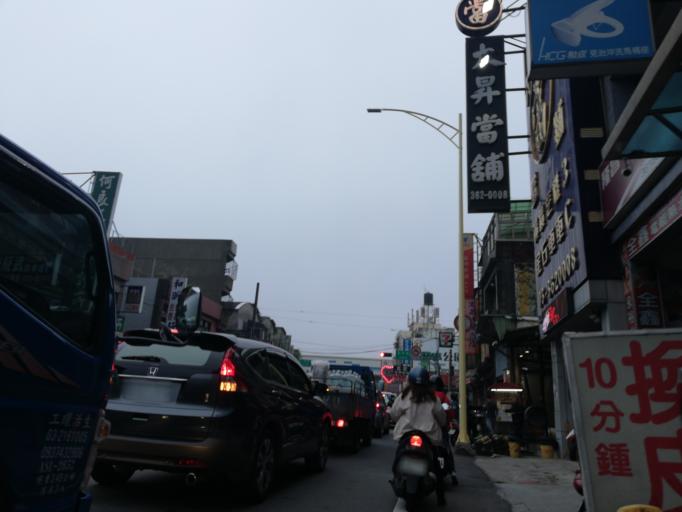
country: TW
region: Taiwan
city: Taoyuan City
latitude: 24.9758
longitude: 121.3024
